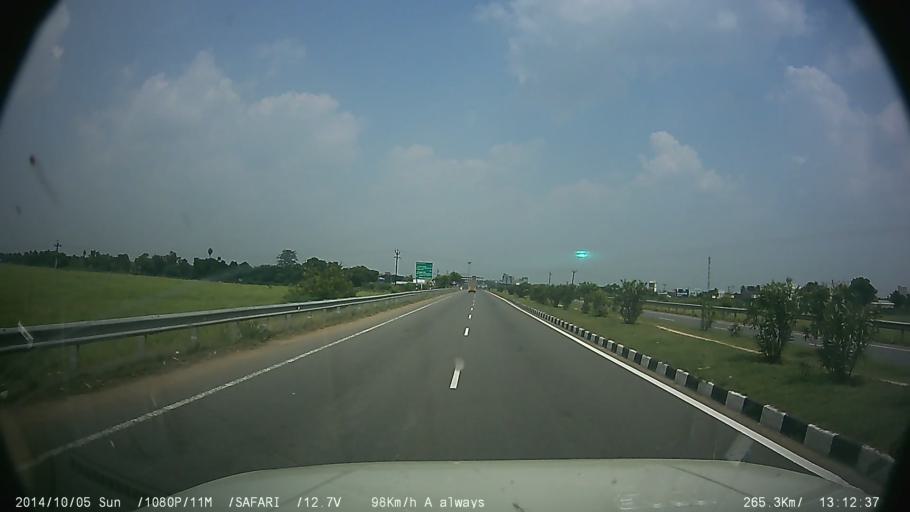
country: IN
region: Tamil Nadu
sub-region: Villupuram
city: Villupuram
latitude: 11.9607
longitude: 79.4933
